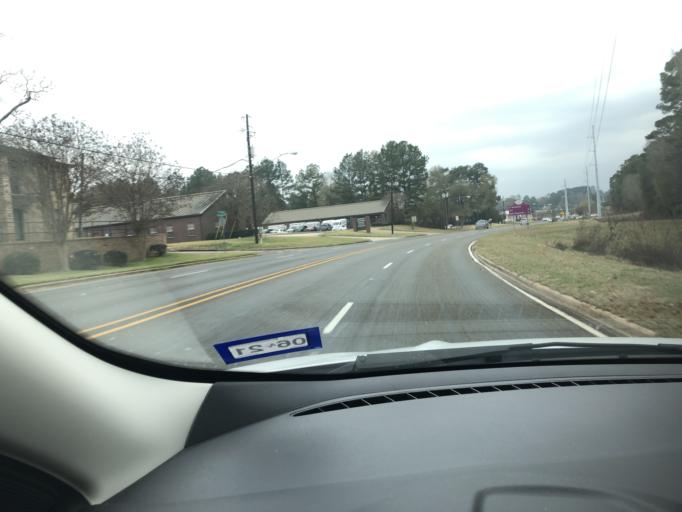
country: US
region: Texas
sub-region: Nacogdoches County
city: Nacogdoches
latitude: 31.6187
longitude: -94.6354
